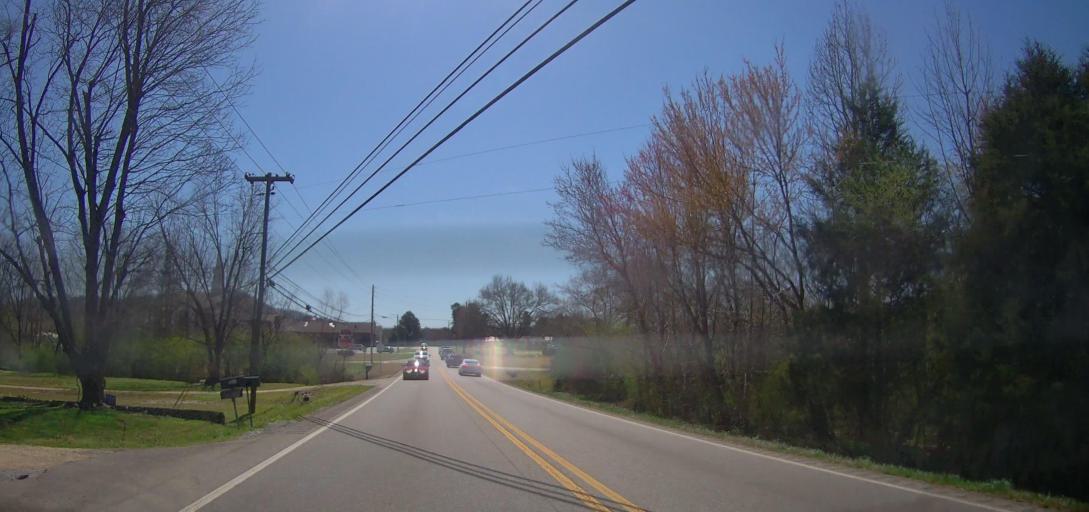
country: US
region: Alabama
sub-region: Etowah County
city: Southside
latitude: 33.8982
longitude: -86.0309
